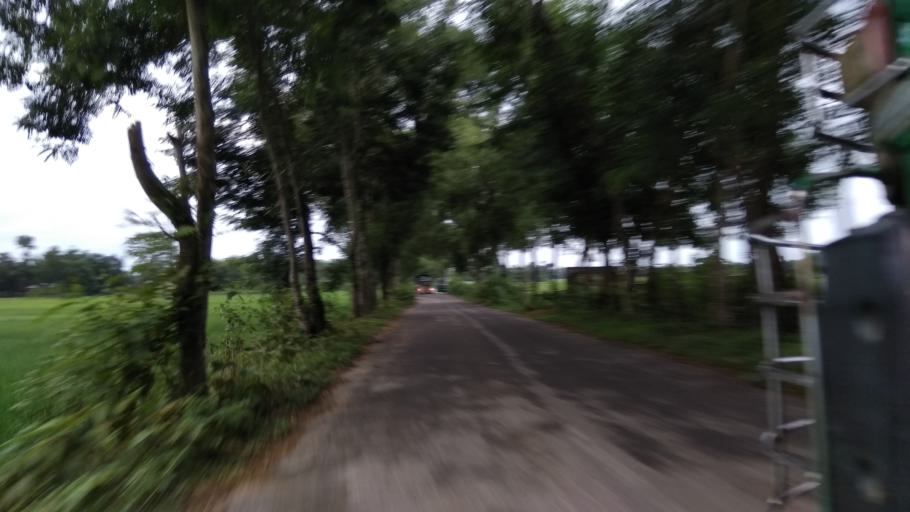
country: IN
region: Tripura
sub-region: Dhalai
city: Kamalpur
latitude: 24.2175
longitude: 91.8544
